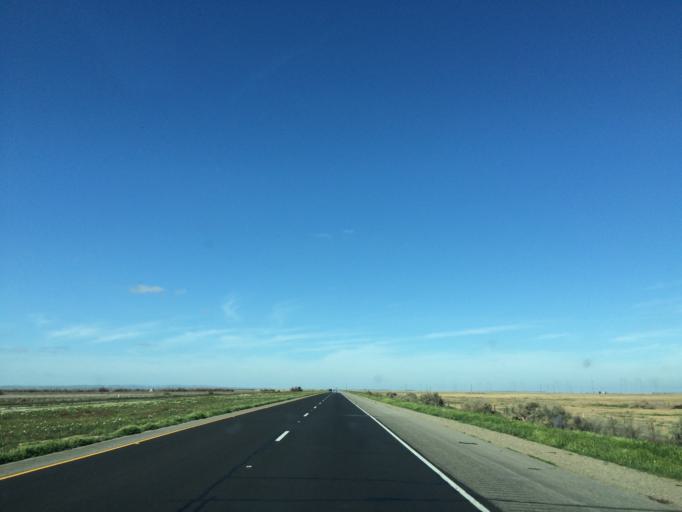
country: US
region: California
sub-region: Kern County
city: Lost Hills
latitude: 35.7978
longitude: -119.7882
